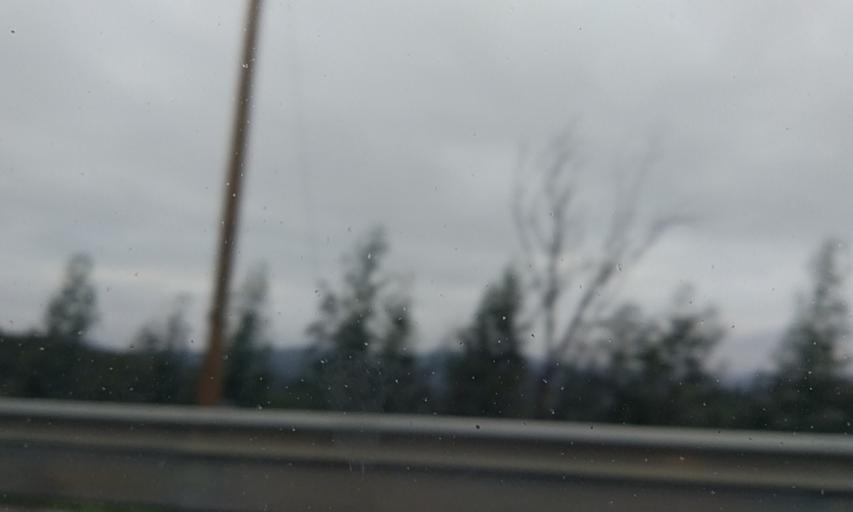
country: PT
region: Viseu
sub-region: Mortagua
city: Mortagua
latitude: 40.3666
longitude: -8.1943
